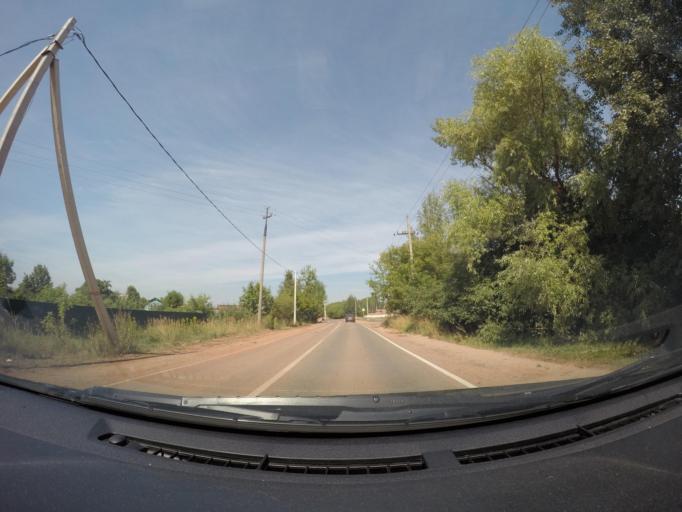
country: RU
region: Moskovskaya
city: Rechitsy
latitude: 55.6236
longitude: 38.4376
